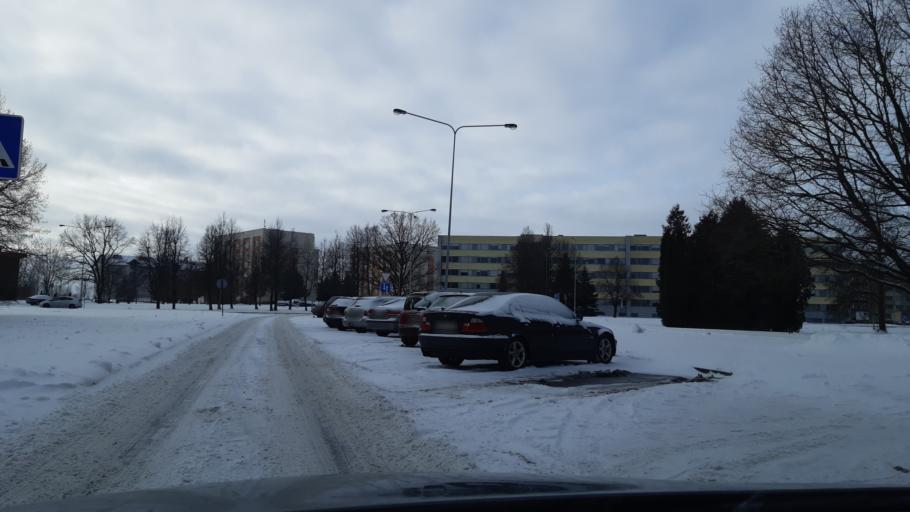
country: LT
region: Kauno apskritis
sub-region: Kauno rajonas
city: Akademija (Kaunas)
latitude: 54.8929
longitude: 23.8304
